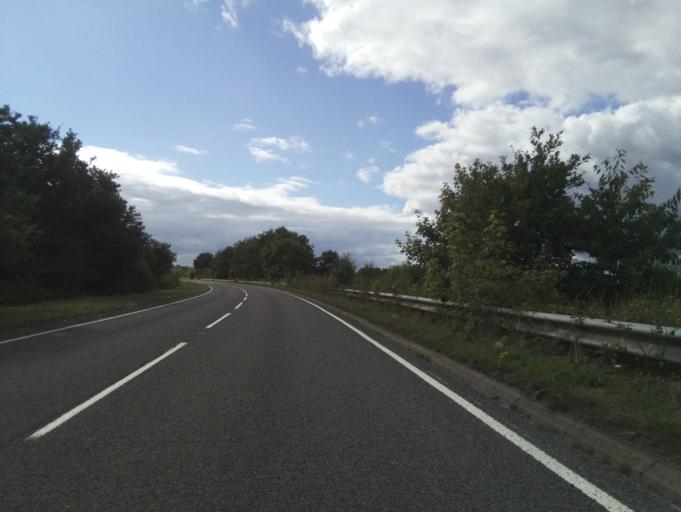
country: GB
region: England
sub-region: Leicestershire
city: Ashby de la Zouch
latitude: 52.7526
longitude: -1.4369
